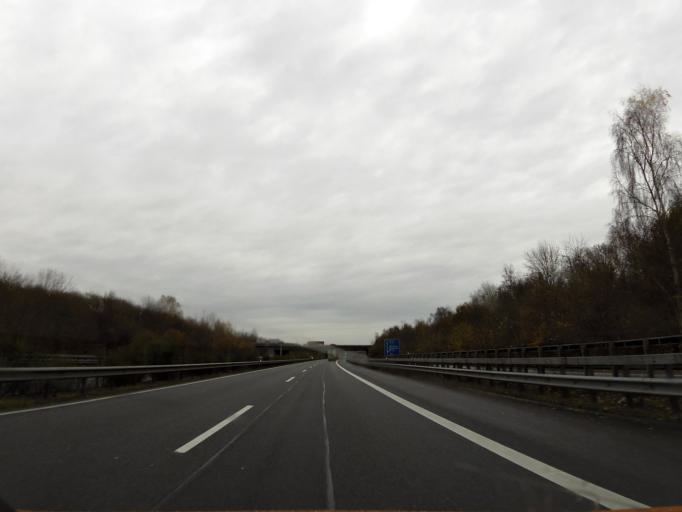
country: DE
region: Lower Saxony
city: Oldenburg
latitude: 53.1154
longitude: 8.2698
